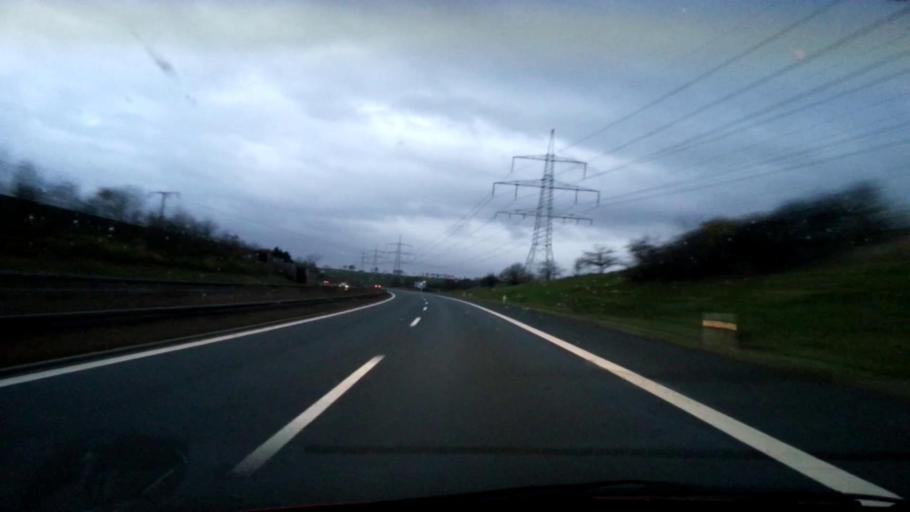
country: DE
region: Bavaria
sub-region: Upper Franconia
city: Schesslitz
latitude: 49.9661
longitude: 10.9945
